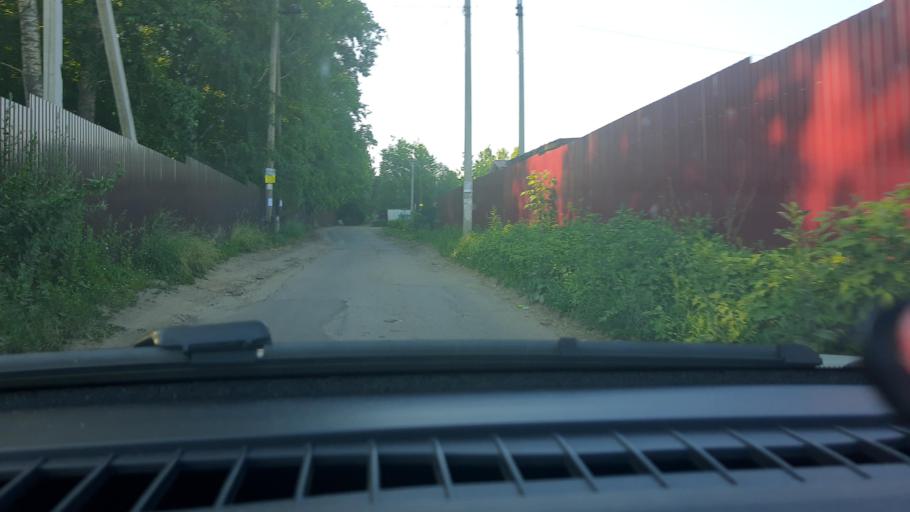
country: RU
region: Nizjnij Novgorod
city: Nizhniy Novgorod
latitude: 56.1913
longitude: 43.9432
